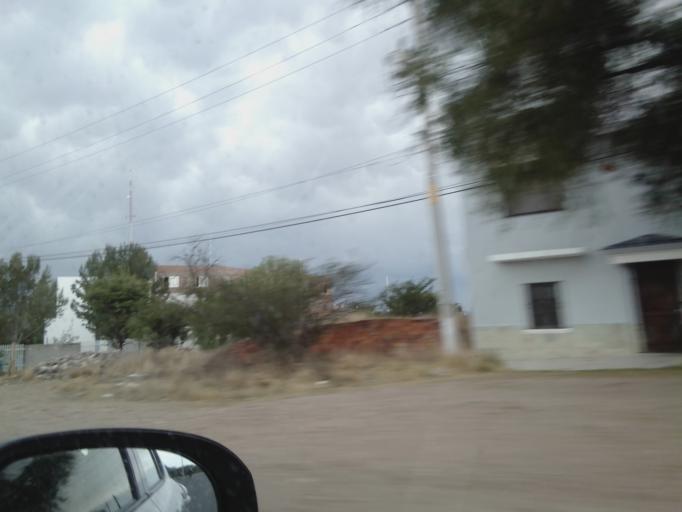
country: MX
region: Guanajuato
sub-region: Dolores Hidalgo Cuna de la Independencia Nacional
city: Colonia Padre Hidalgo
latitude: 21.1703
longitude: -100.9324
